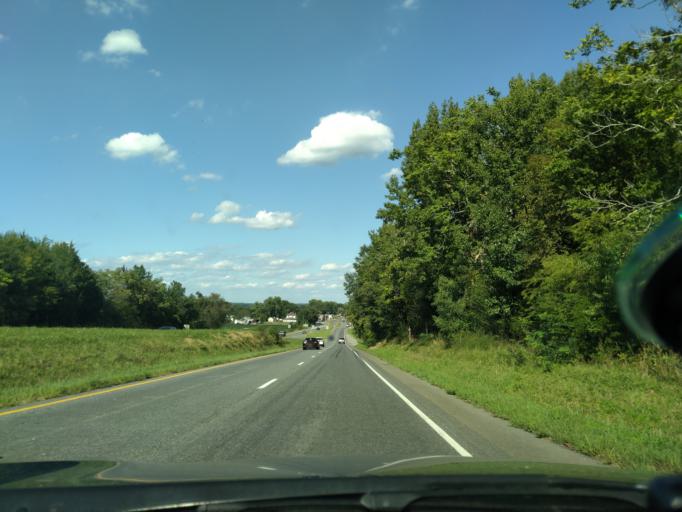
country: US
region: Virginia
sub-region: King George County
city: King George
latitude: 38.1595
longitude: -77.2035
